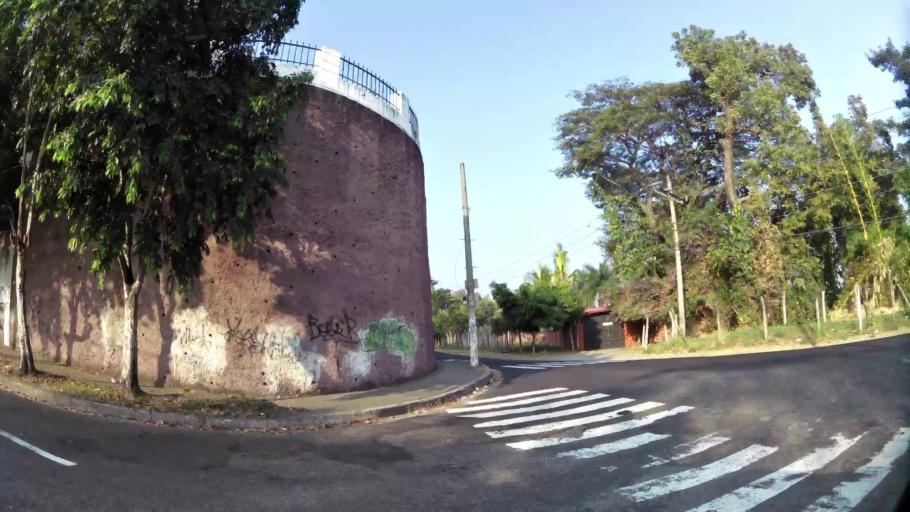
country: SV
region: San Salvador
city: San Salvador
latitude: 13.6846
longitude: -89.2024
